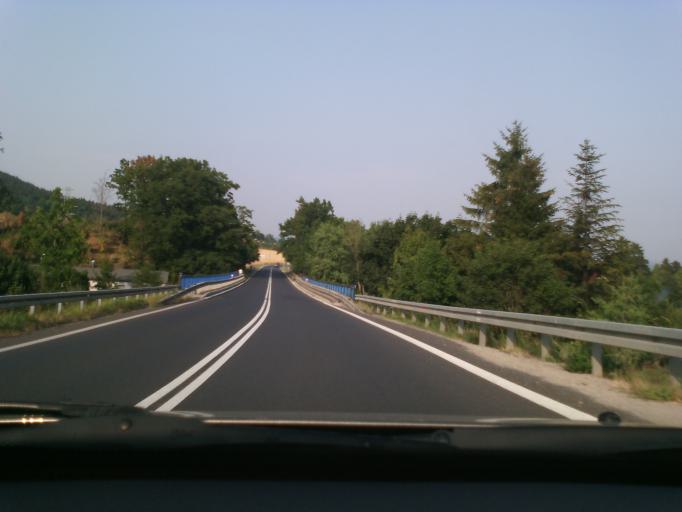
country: PL
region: Lower Silesian Voivodeship
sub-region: Powiat jeleniogorski
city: Piechowice
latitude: 50.8512
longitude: 15.5809
